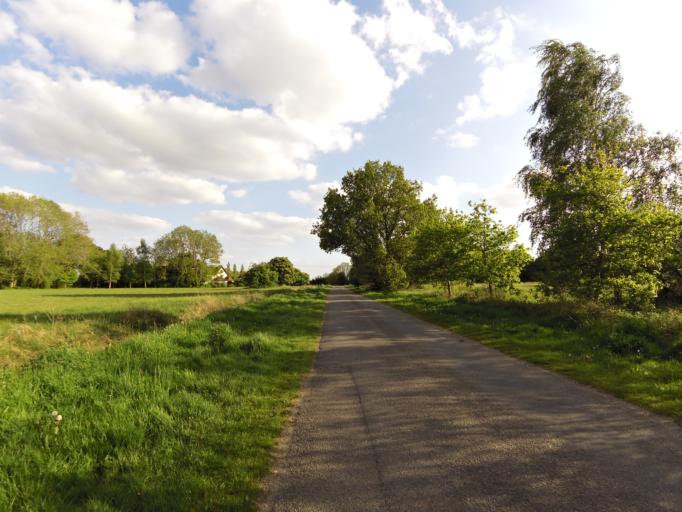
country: GB
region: England
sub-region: Suffolk
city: Halesworth
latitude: 52.4060
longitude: 1.5073
